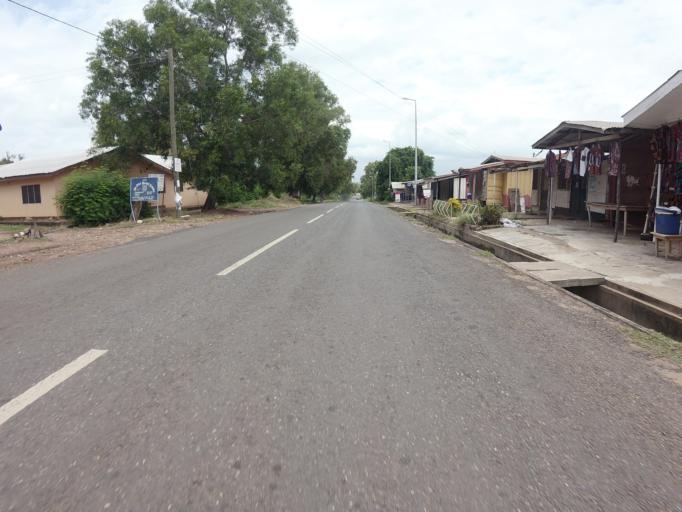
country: GH
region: Volta
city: Ho
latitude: 6.5925
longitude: 0.4625
